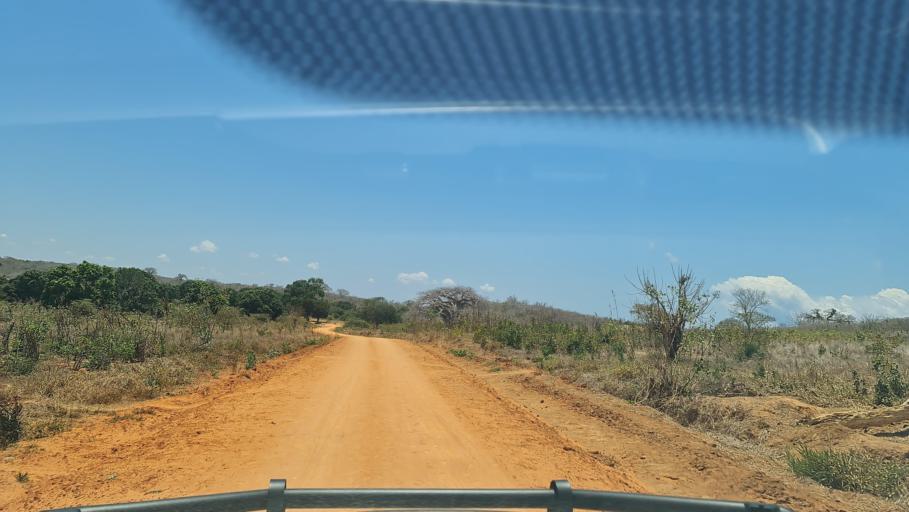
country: MZ
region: Nampula
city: Nacala
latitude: -14.2125
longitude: 40.6785
